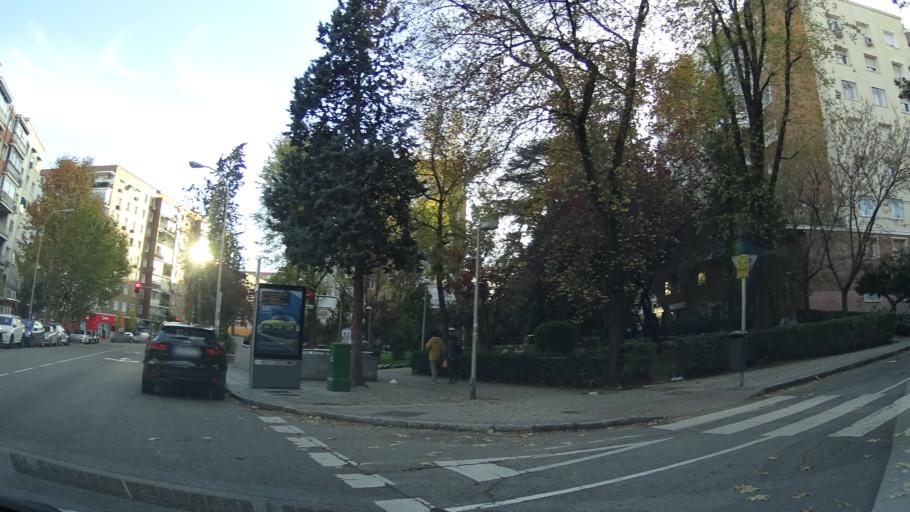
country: ES
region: Madrid
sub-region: Provincia de Madrid
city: Salamanca
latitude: 40.4397
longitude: -3.6630
